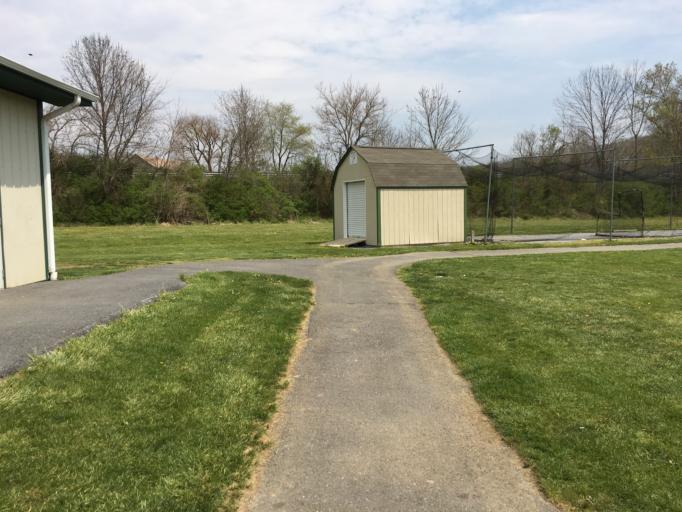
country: US
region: Maryland
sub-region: Frederick County
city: Myersville
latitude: 39.5091
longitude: -77.5595
